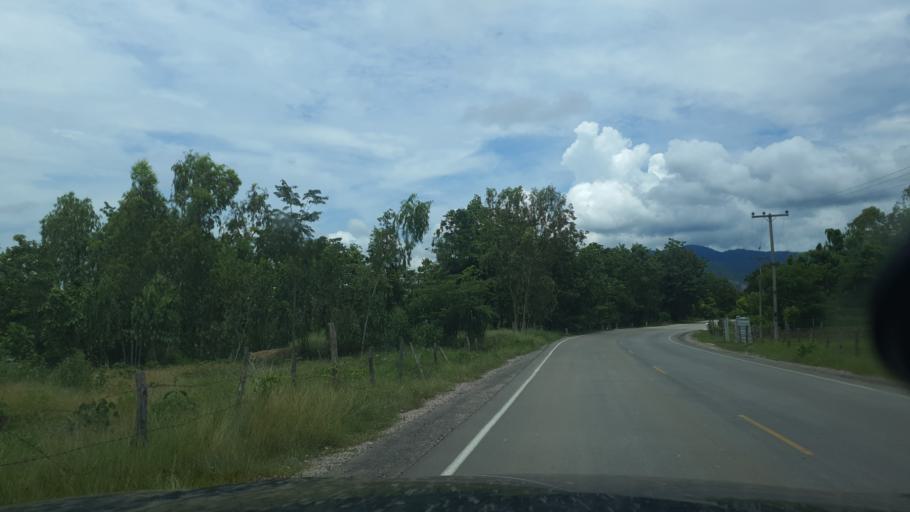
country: TH
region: Lampang
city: Sop Prap
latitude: 17.9139
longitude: 99.3927
